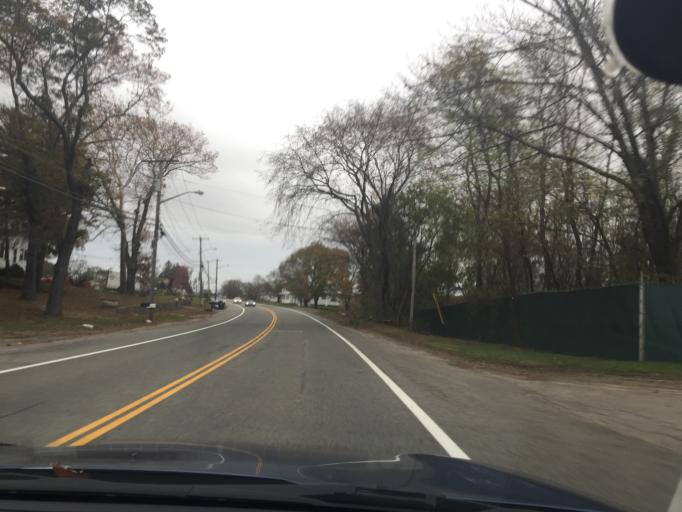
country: US
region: Rhode Island
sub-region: Providence County
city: Johnston
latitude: 41.7918
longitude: -71.5314
